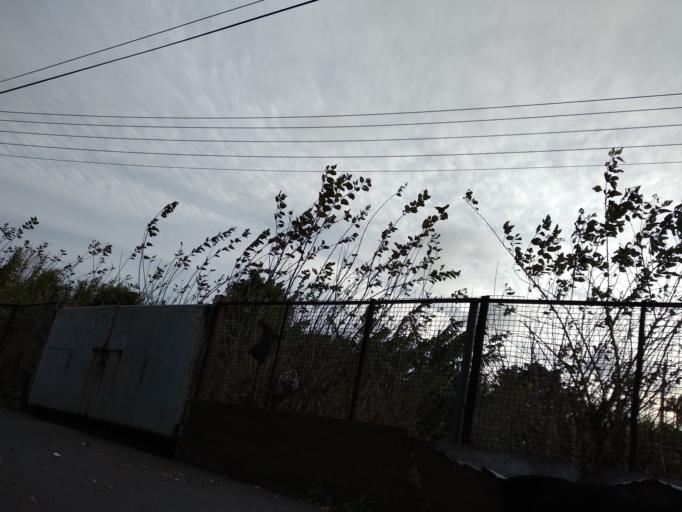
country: TW
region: Taiwan
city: Daxi
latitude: 24.9417
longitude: 121.2003
